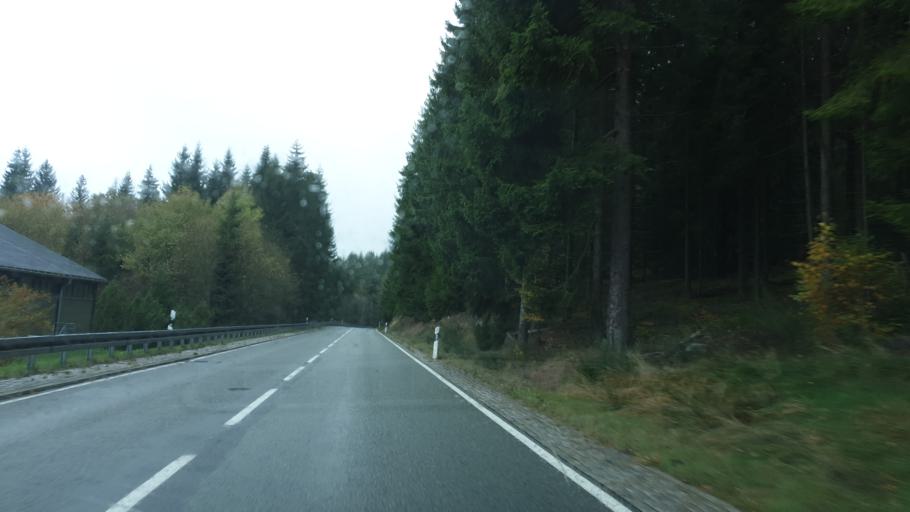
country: DE
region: Saxony
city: Muldenhammer
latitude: 50.4691
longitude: 12.4986
